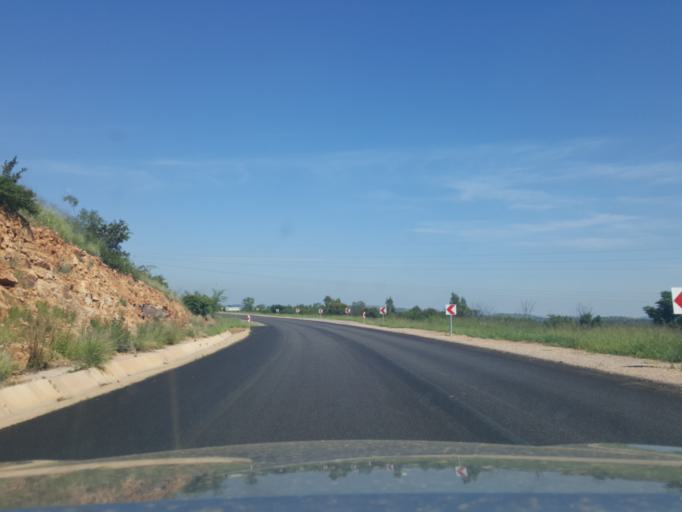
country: ZA
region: Gauteng
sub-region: City of Tshwane Metropolitan Municipality
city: Cullinan
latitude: -25.6782
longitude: 28.5052
